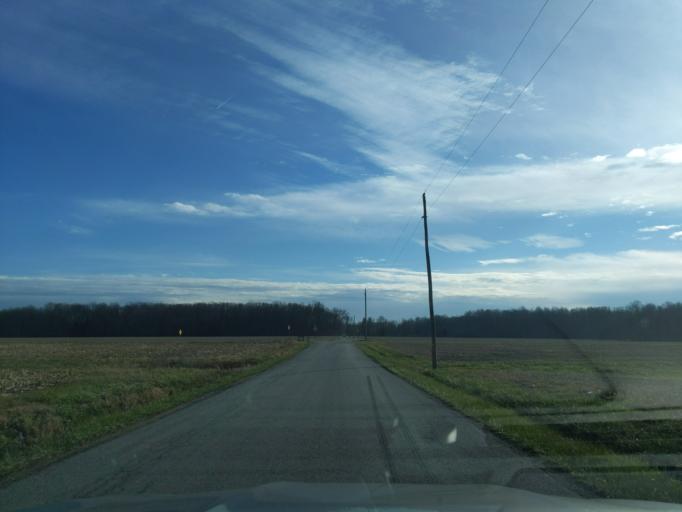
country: US
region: Indiana
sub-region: Decatur County
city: Westport
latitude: 39.1911
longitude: -85.4613
